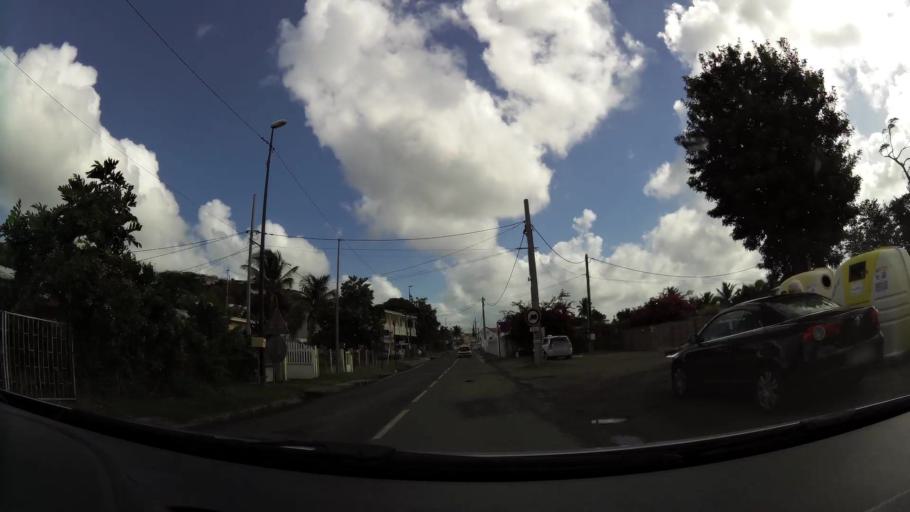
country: MQ
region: Martinique
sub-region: Martinique
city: Les Trois-Ilets
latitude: 14.4790
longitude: -61.0294
